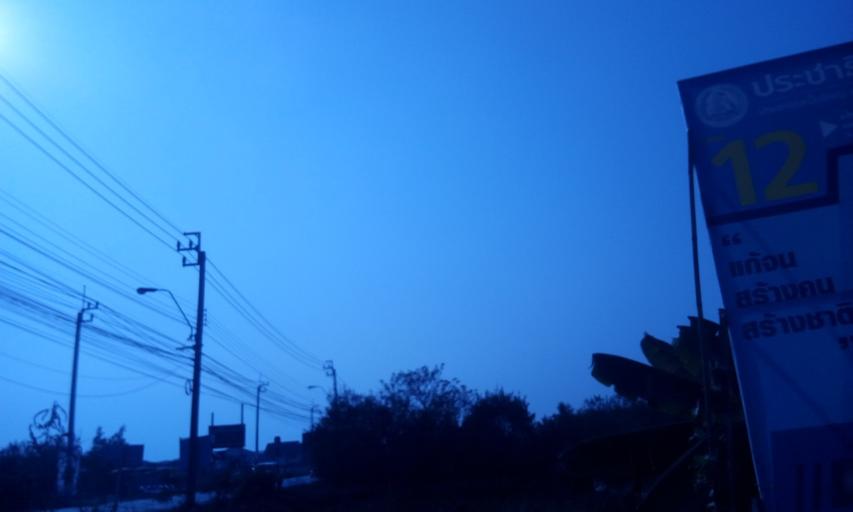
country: TH
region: Nonthaburi
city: Sai Noi
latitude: 13.9725
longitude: 100.3181
